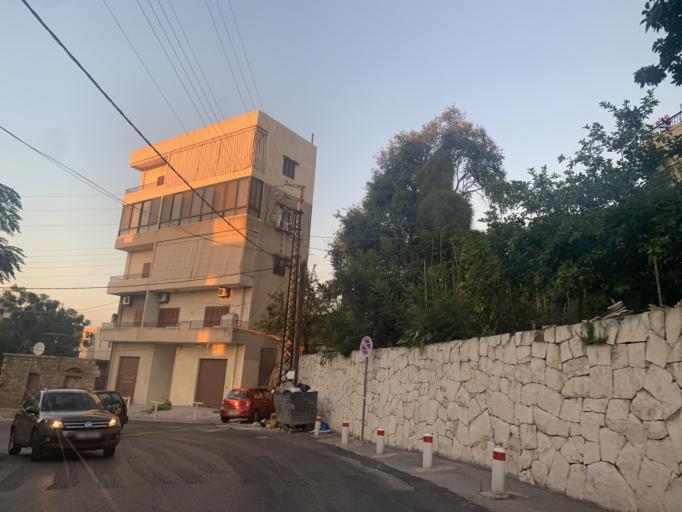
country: LB
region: Mont-Liban
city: Djounie
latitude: 33.9715
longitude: 35.6270
